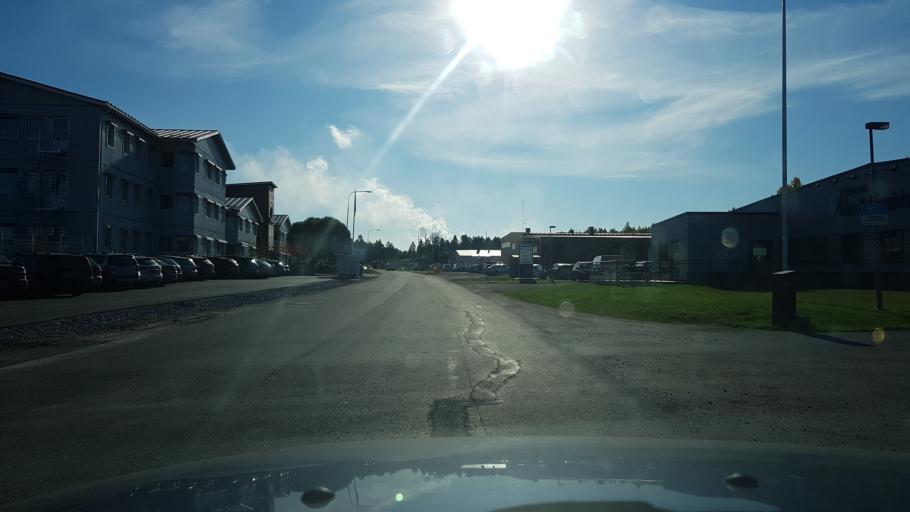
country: SE
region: Norrbotten
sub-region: Pitea Kommun
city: Bergsviken
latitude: 65.3382
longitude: 21.4122
